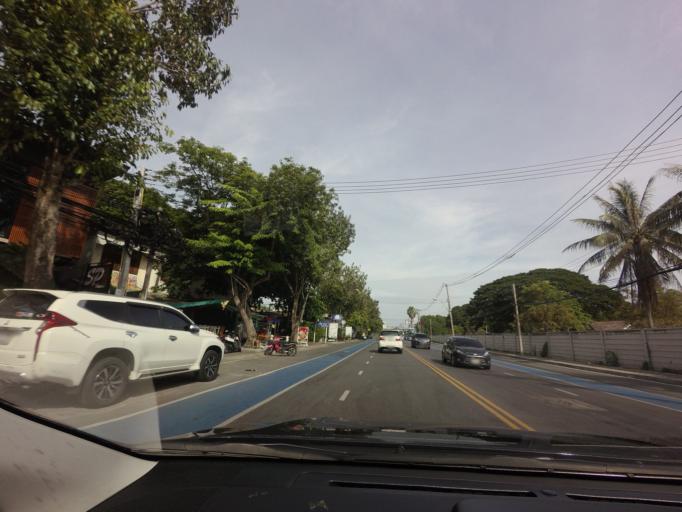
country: TH
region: Chon Buri
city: Chon Buri
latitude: 13.2874
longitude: 100.9159
